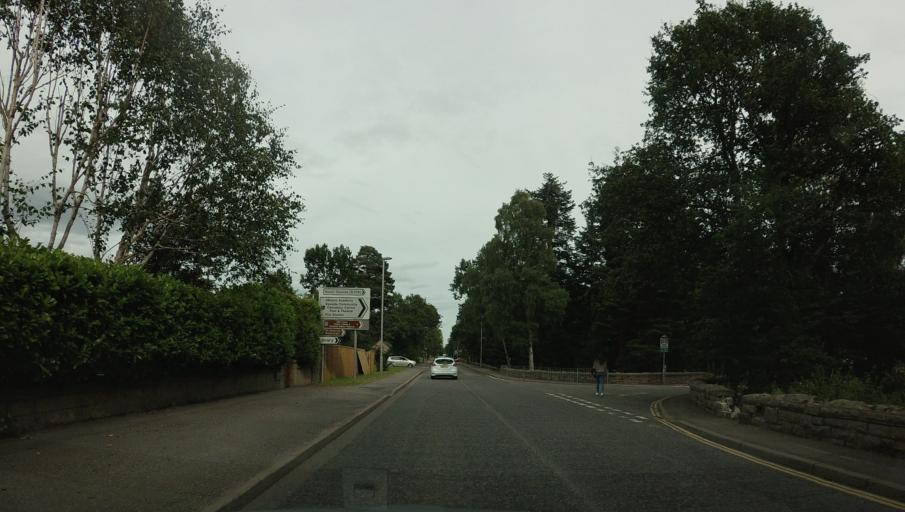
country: GB
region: Scotland
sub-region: Aberdeenshire
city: Aboyne
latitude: 57.0760
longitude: -2.7947
